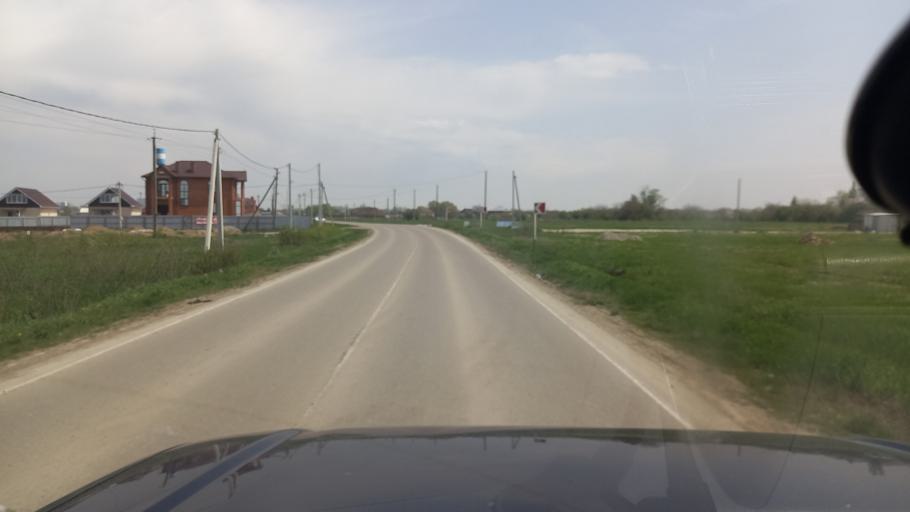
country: RU
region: Adygeya
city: Yablonovskiy
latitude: 44.9868
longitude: 38.9874
